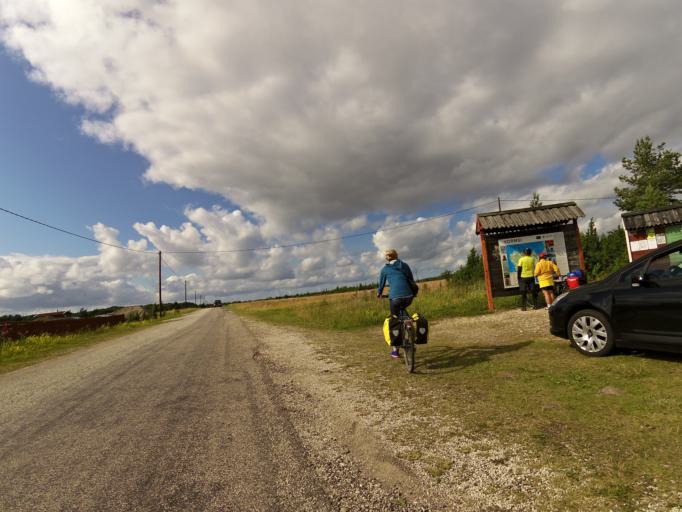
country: EE
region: Laeaene
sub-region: Vormsi vald
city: Hullo
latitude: 58.9735
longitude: 23.3135
